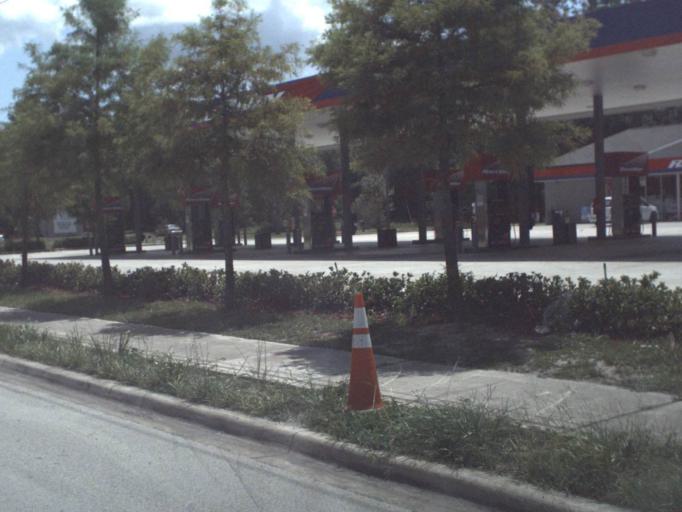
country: US
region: Florida
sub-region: Alachua County
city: Waldo
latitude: 29.7963
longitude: -82.1676
